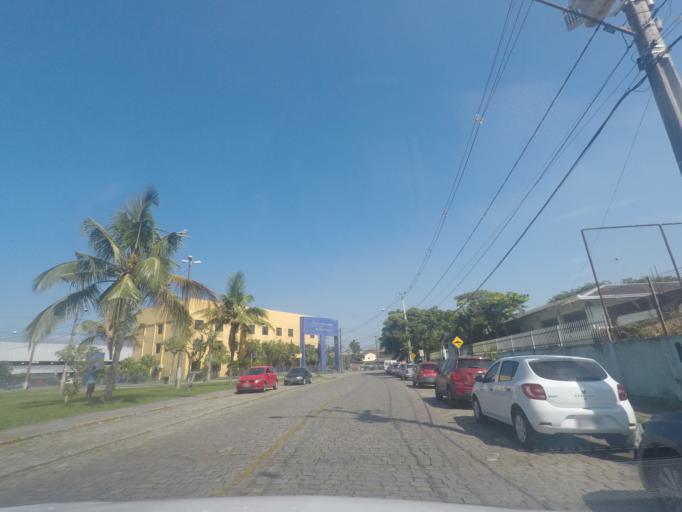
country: BR
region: Parana
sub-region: Paranagua
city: Paranagua
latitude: -25.5235
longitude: -48.5091
